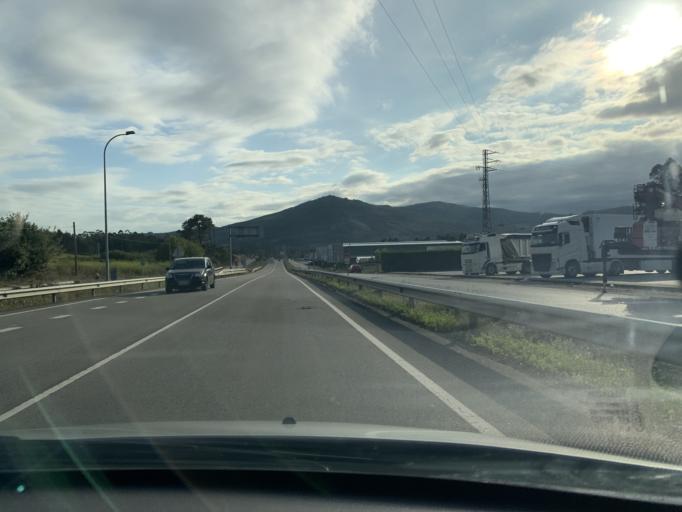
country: ES
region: Galicia
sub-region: Provincia de Lugo
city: Barreiros
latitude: 43.5392
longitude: -7.2532
